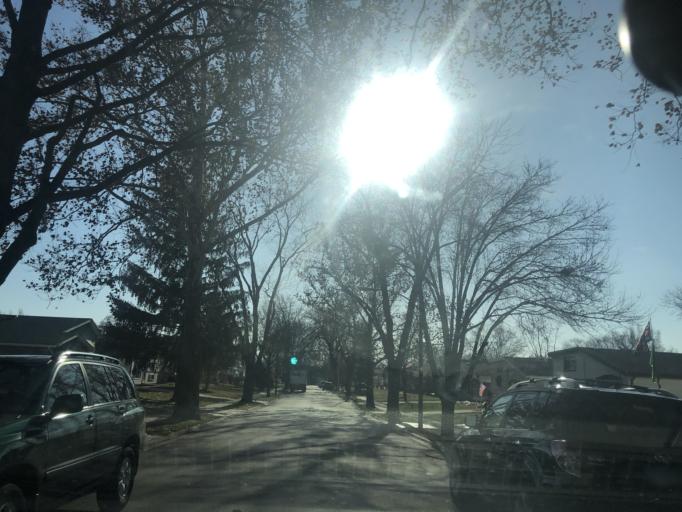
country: US
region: Illinois
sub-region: DuPage County
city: Addison
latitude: 41.9290
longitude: -87.9947
